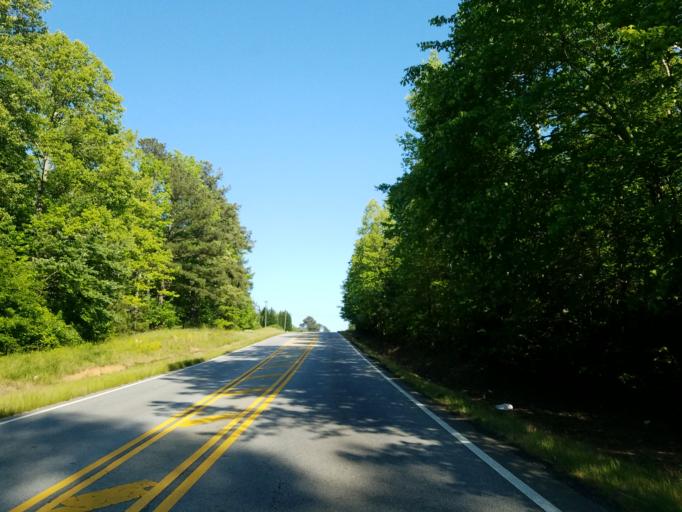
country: US
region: Georgia
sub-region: Carroll County
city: Villa Rica
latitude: 33.7648
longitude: -84.9521
